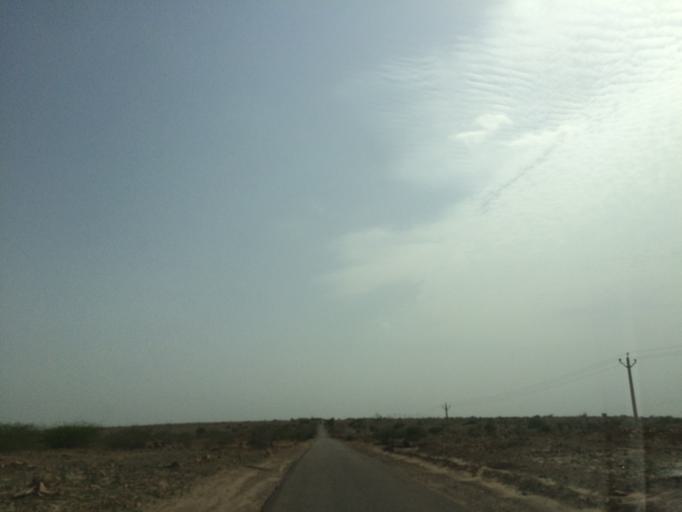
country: IN
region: Rajasthan
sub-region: Jaisalmer
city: Jaisalmer
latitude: 26.8892
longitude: 70.9172
